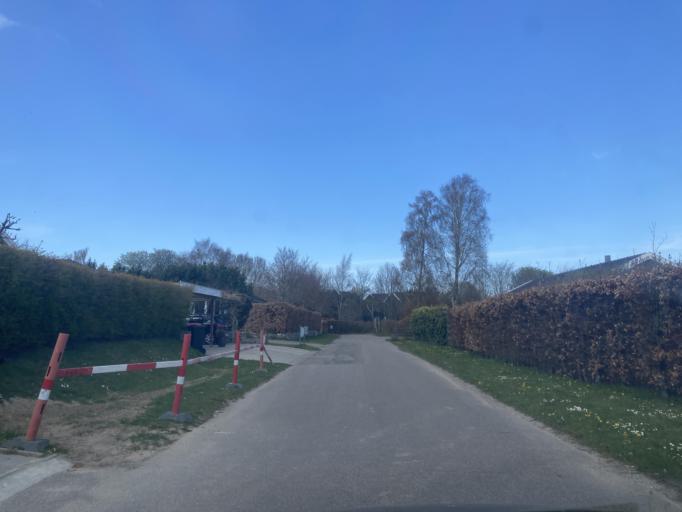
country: DK
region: Capital Region
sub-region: Gribskov Kommune
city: Helsinge
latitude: 56.0646
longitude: 12.1147
